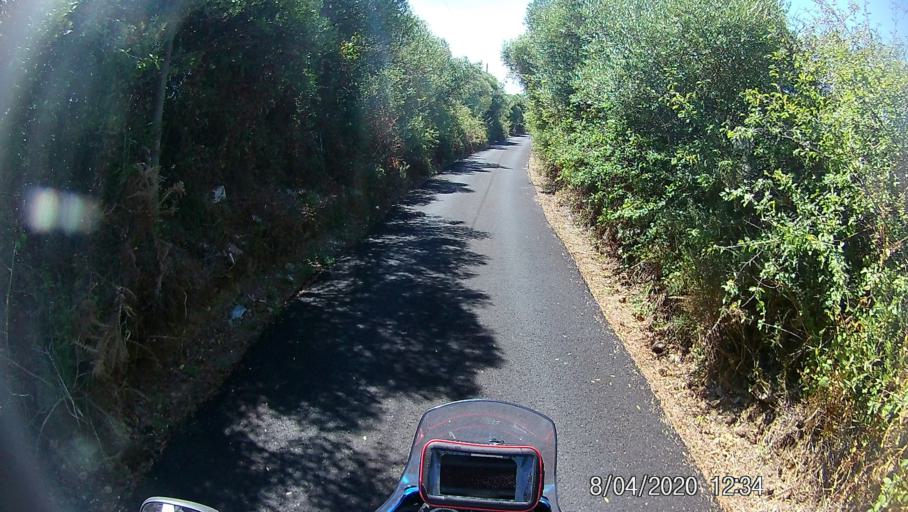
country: PT
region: Lisbon
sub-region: Sintra
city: Rio de Mouro
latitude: 38.7520
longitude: -9.3609
